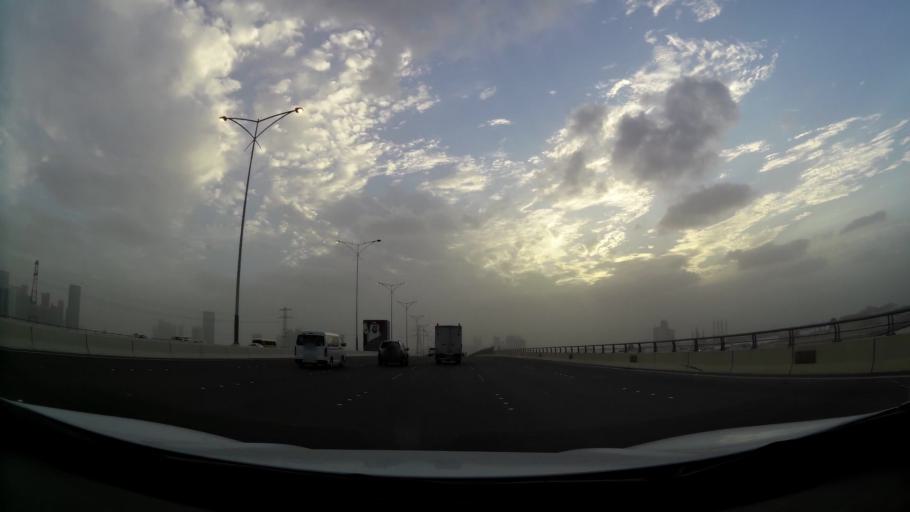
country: AE
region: Abu Dhabi
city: Abu Dhabi
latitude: 24.5227
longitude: 54.4033
